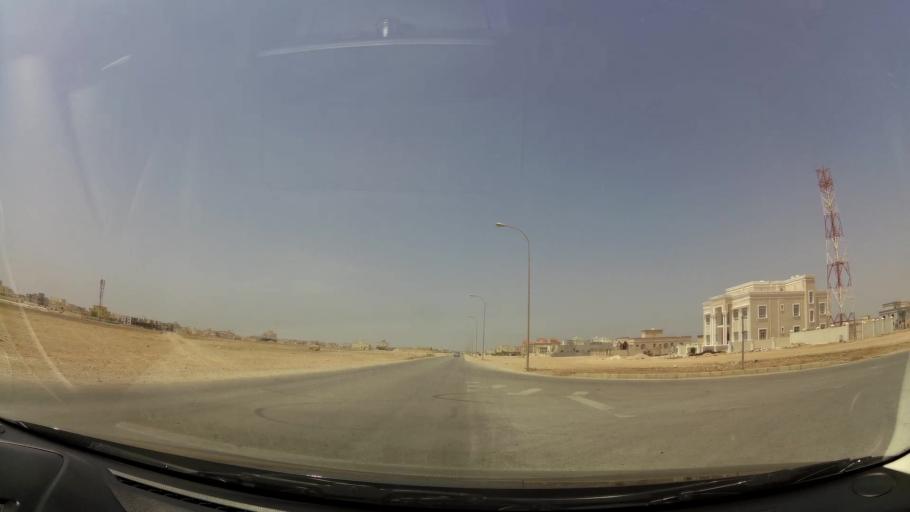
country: OM
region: Zufar
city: Salalah
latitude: 17.0821
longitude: 54.2054
